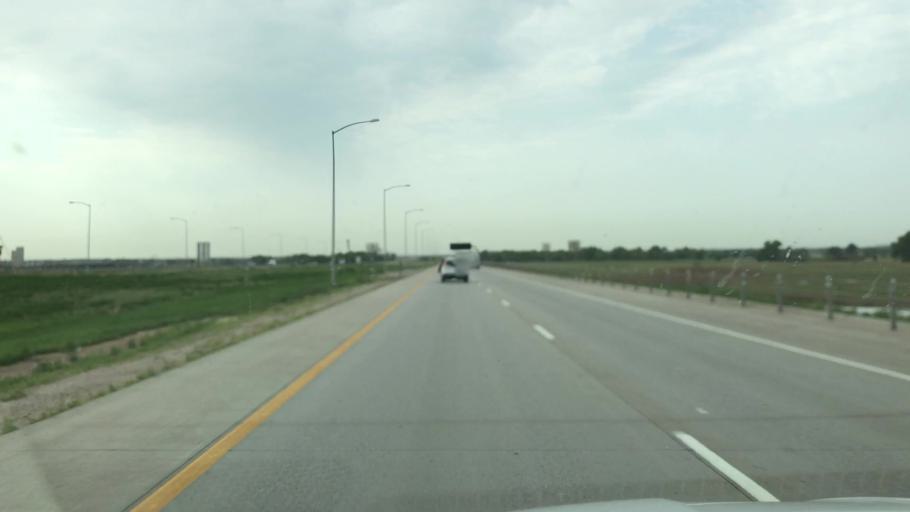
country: US
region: Colorado
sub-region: Adams County
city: Aurora
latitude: 39.8177
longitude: -104.7872
